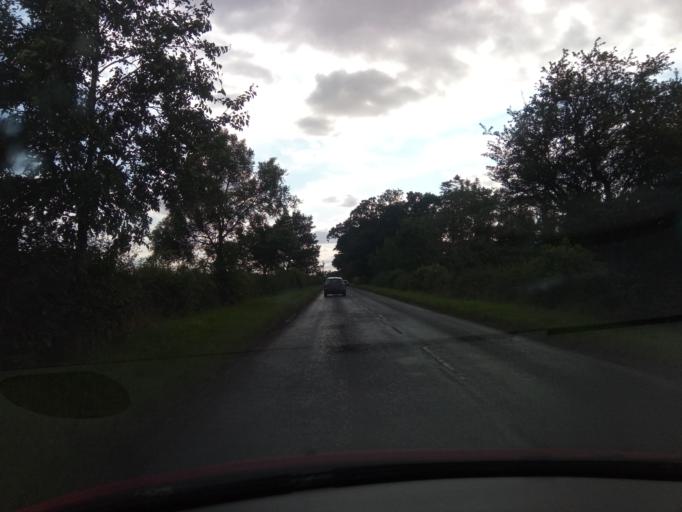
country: GB
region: Scotland
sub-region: The Scottish Borders
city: Coldstream
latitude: 55.6964
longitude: -2.3212
